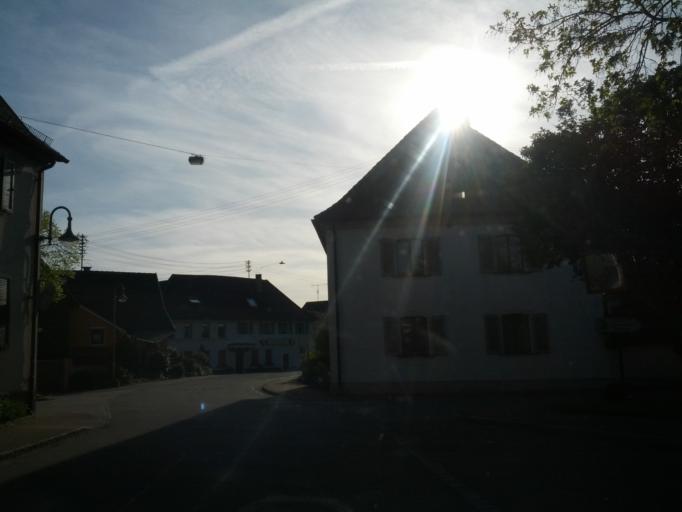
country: DE
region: Baden-Wuerttemberg
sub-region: Freiburg Region
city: Eichstetten
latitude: 48.1066
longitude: 7.7762
